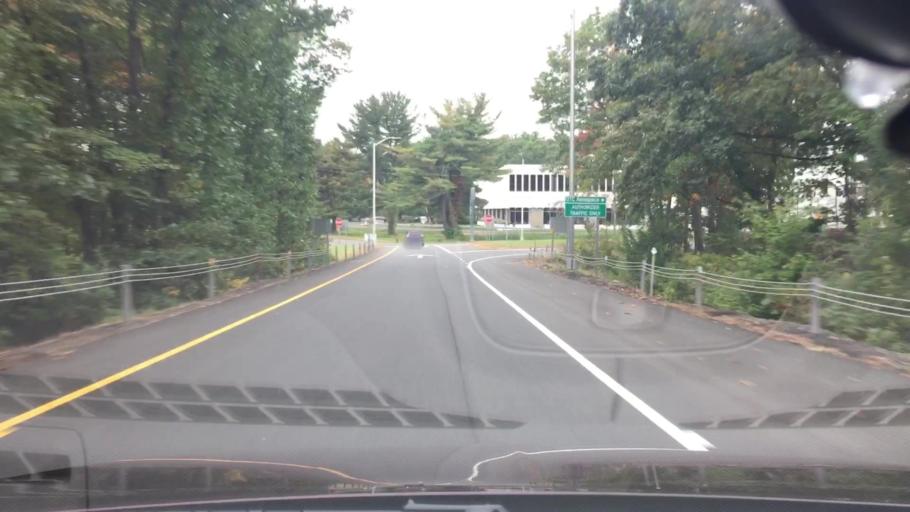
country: US
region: Connecticut
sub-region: Hartford County
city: Windsor Locks
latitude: 41.9184
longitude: -72.6836
